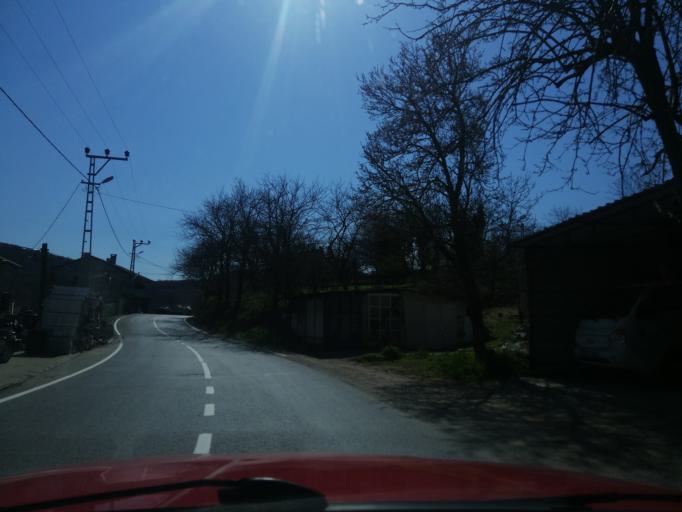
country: TR
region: Istanbul
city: Mahmut Sevket Pasa
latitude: 41.1265
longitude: 29.1582
